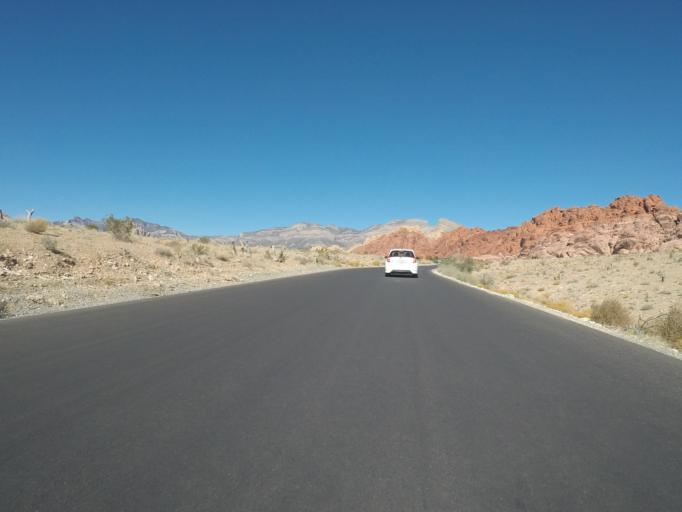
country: US
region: Nevada
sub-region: Clark County
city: Summerlin South
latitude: 36.1427
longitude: -115.4285
